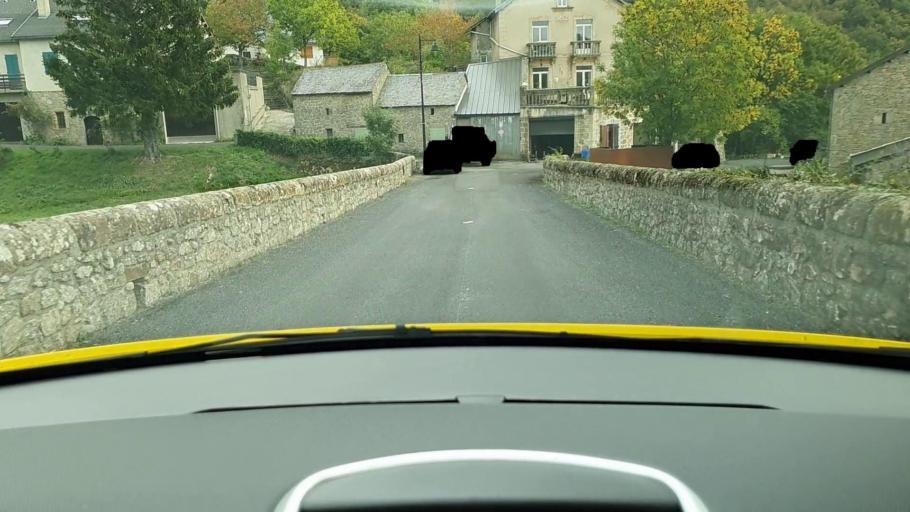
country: FR
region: Languedoc-Roussillon
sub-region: Departement de la Lozere
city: Meyrueis
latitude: 44.0643
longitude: 3.4466
